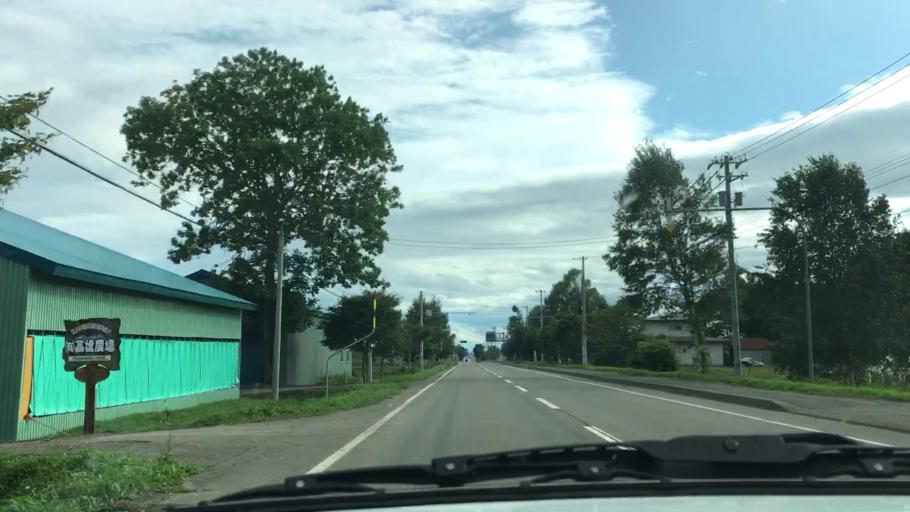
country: JP
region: Hokkaido
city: Otofuke
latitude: 43.2421
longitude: 143.2972
